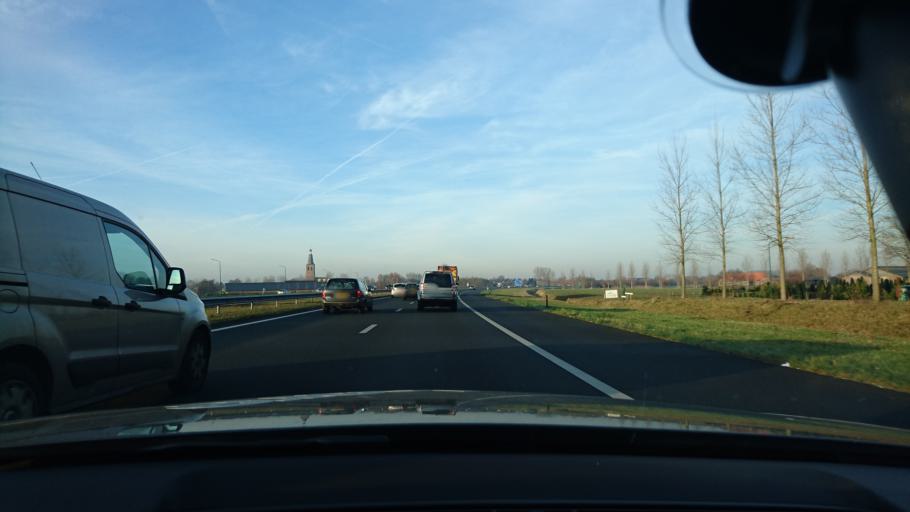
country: NL
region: North Brabant
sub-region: Gemeente Sint-Oedenrode
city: Sint-Oedenrode
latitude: 51.5601
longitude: 5.4747
